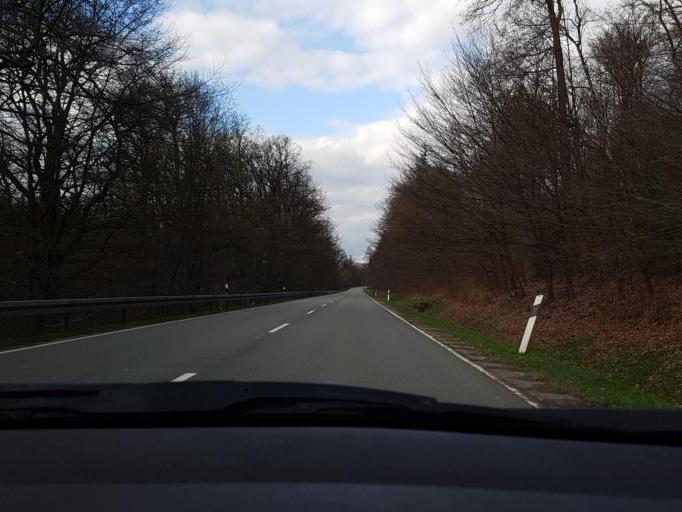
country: DE
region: Lower Saxony
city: Derental
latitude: 51.7344
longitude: 9.5132
